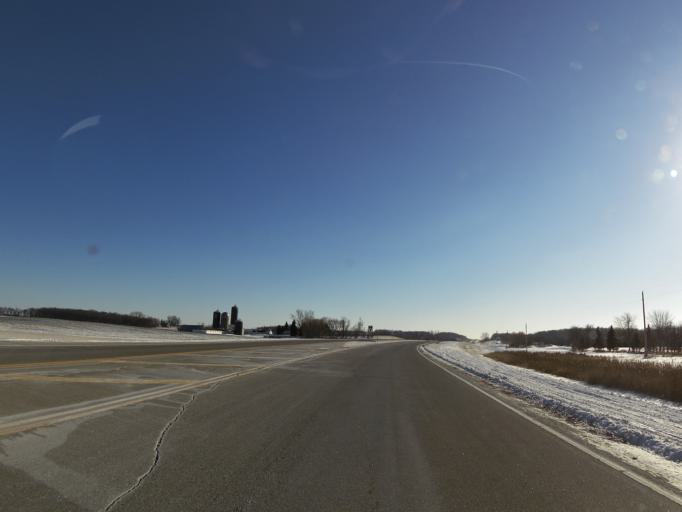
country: US
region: Minnesota
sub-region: Le Sueur County
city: New Prague
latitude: 44.5663
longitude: -93.5021
